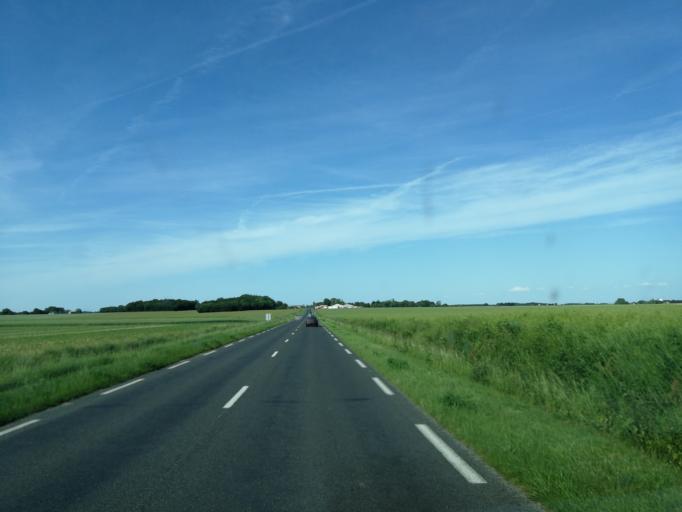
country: FR
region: Centre
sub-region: Departement d'Indre-et-Loire
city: Monnaie
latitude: 47.5247
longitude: 0.8275
